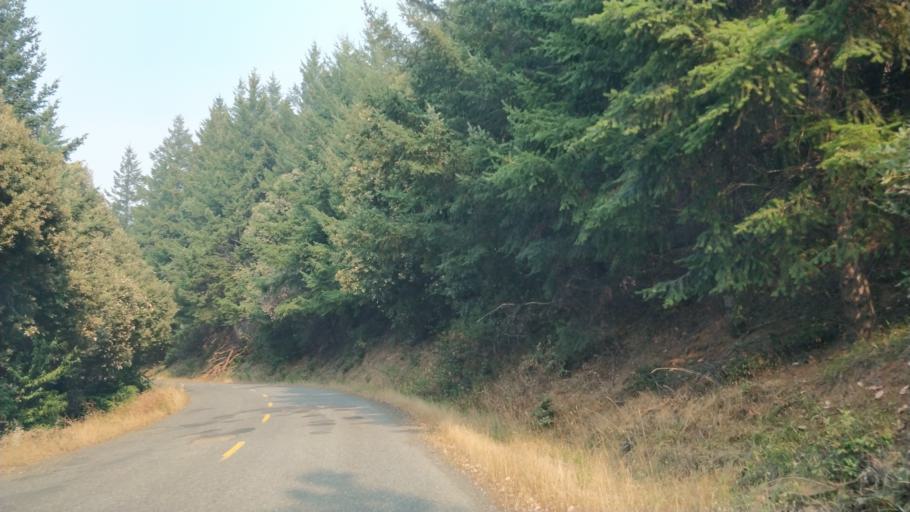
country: US
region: California
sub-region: Humboldt County
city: Rio Dell
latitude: 40.2619
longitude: -124.1146
